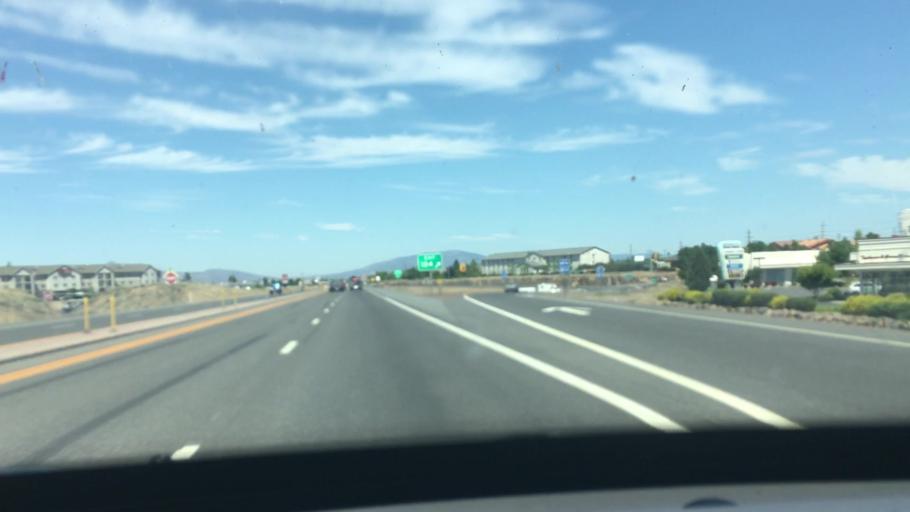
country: US
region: Oregon
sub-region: Deschutes County
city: Redmond
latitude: 44.2402
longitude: -121.1953
